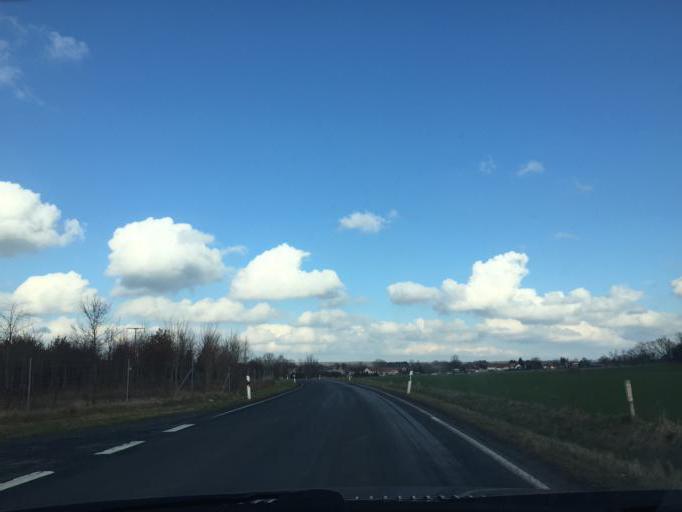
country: DE
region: Saxony
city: Thiendorf
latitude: 51.2862
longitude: 13.7357
